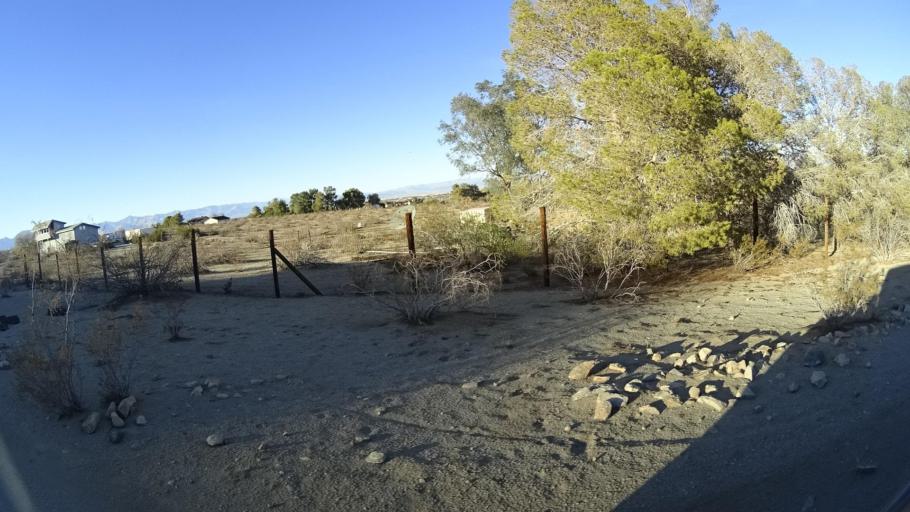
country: US
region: California
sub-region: Kern County
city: Ridgecrest
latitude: 35.5786
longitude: -117.6587
